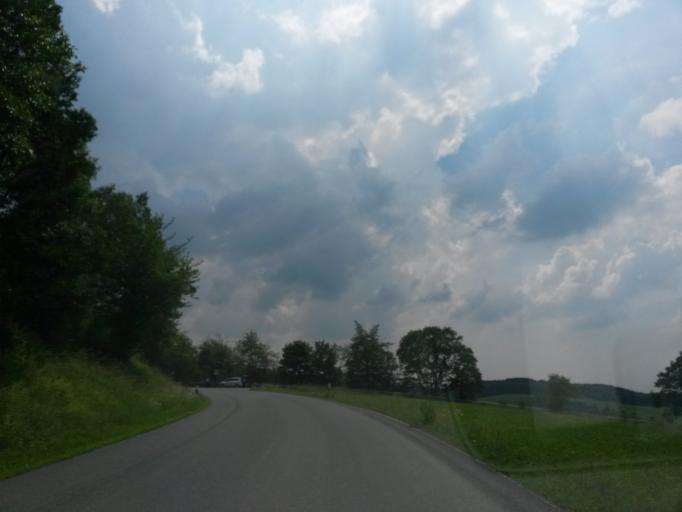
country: DE
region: North Rhine-Westphalia
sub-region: Regierungsbezirk Arnsberg
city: Attendorn
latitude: 51.0686
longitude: 7.9070
